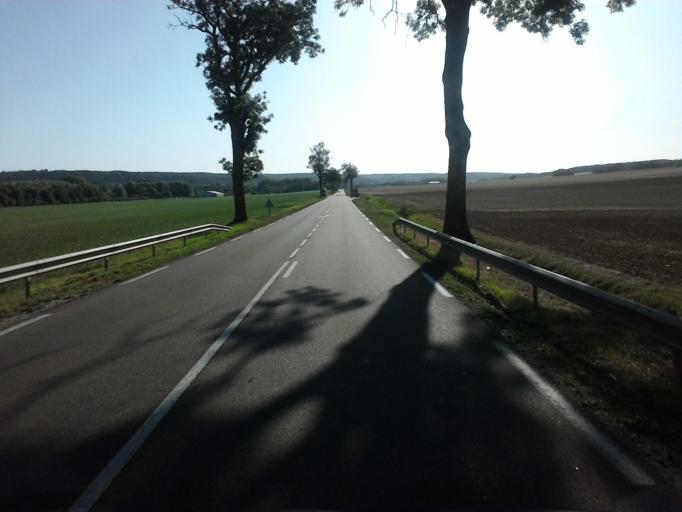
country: FR
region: Champagne-Ardenne
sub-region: Departement de l'Aube
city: Bar-sur-Seine
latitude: 48.1288
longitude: 4.3440
